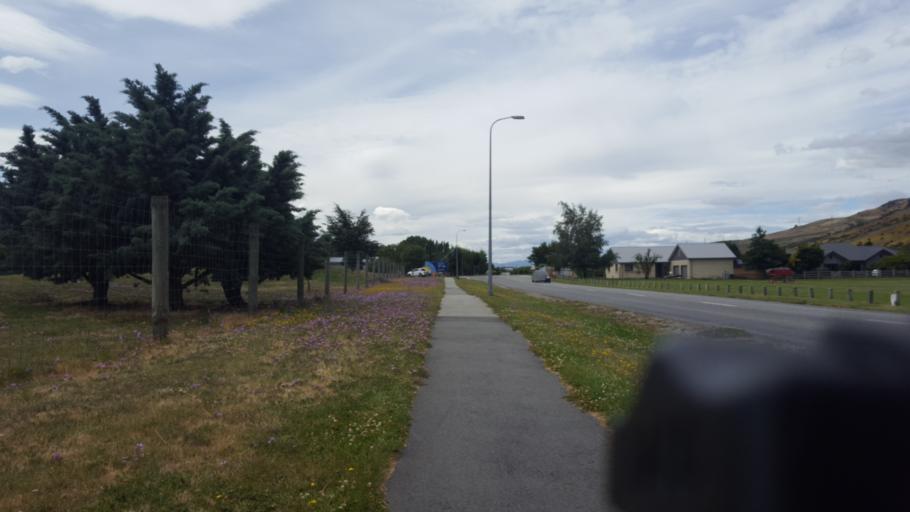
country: NZ
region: Otago
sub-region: Queenstown-Lakes District
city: Wanaka
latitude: -45.0414
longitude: 169.2143
